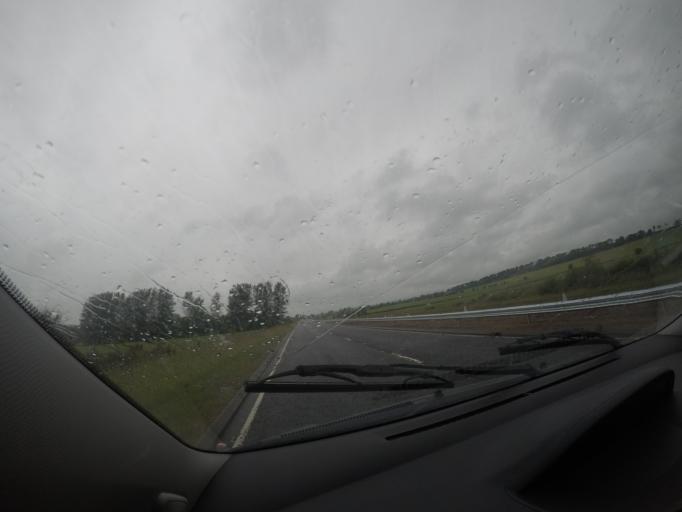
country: GB
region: Scotland
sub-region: Angus
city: Brechin
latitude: 56.7250
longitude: -2.7283
